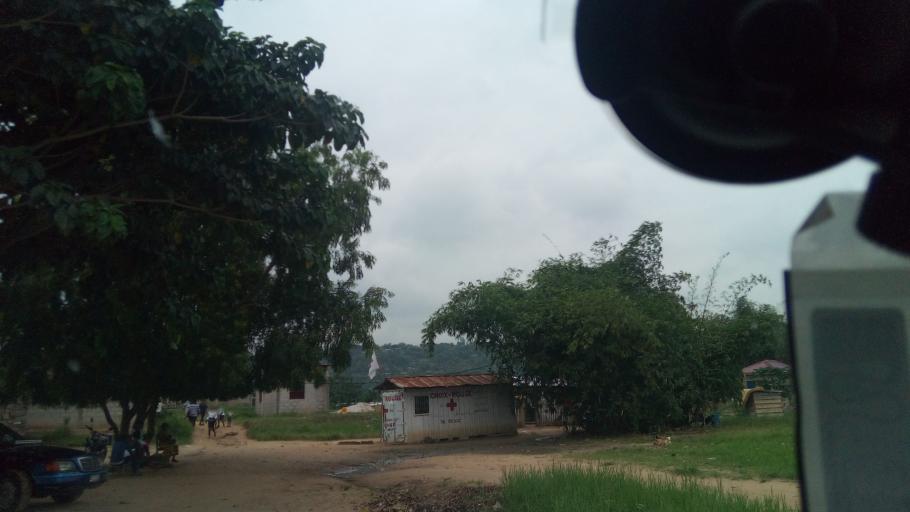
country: CG
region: Brazzaville
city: Brazzaville
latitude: -4.0568
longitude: 15.5555
